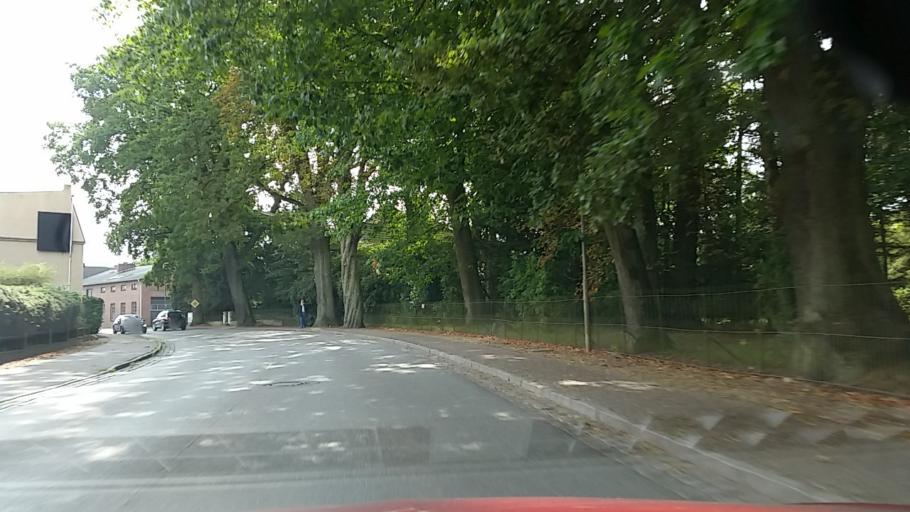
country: DE
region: Schleswig-Holstein
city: Halstenbek
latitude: 53.6023
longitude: 9.8188
